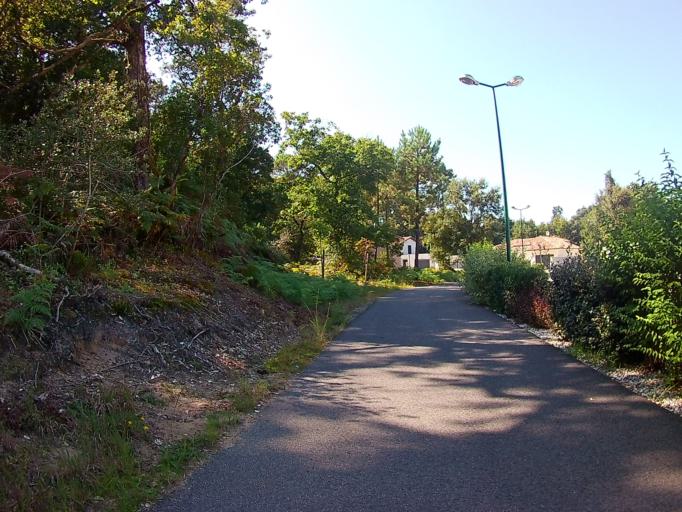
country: FR
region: Aquitaine
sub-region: Departement des Landes
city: Labenne
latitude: 43.5916
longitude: -1.4360
